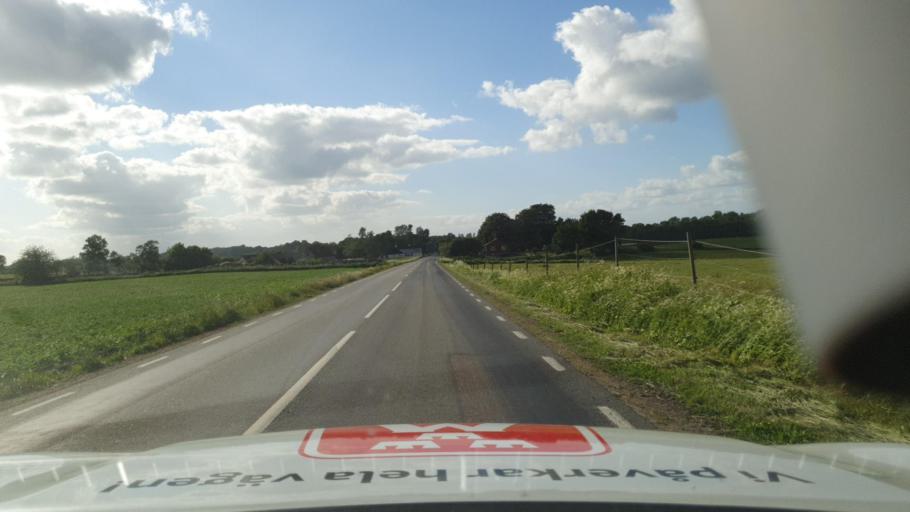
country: SE
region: Skane
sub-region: Tomelilla Kommun
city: Tomelilla
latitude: 55.5884
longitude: 14.0996
